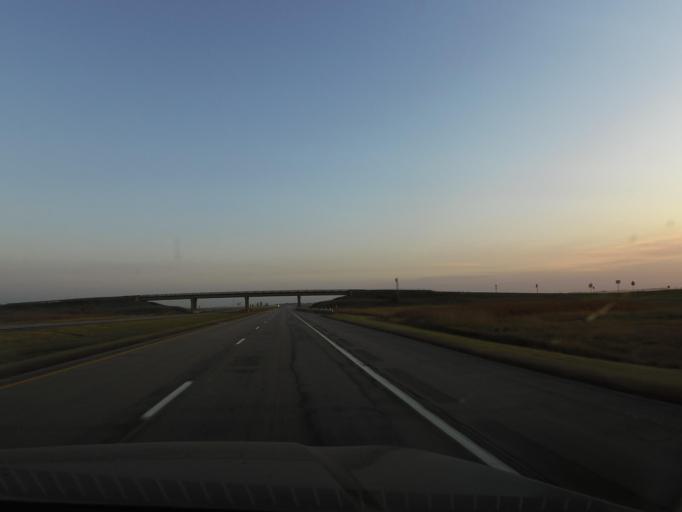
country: US
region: Minnesota
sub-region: Kittson County
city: Hallock
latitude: 48.7038
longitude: -97.1901
